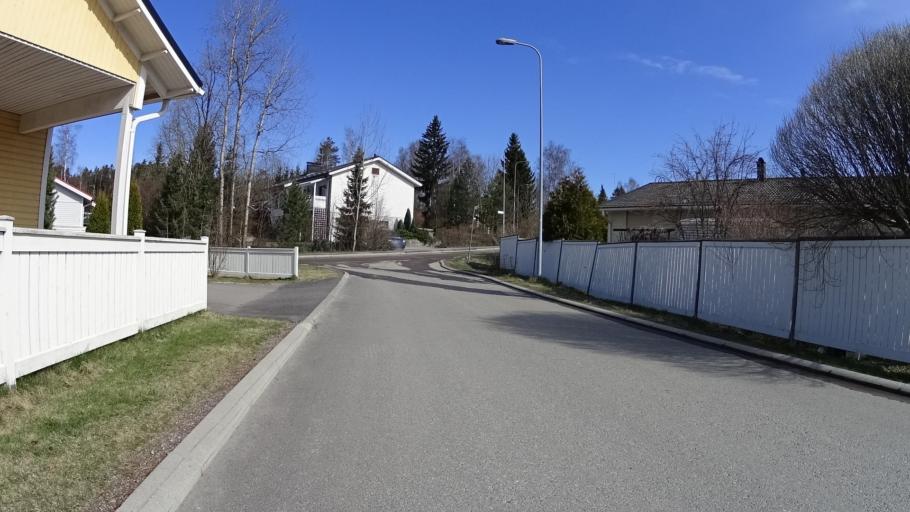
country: FI
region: Uusimaa
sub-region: Helsinki
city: Kilo
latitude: 60.2413
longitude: 24.7806
